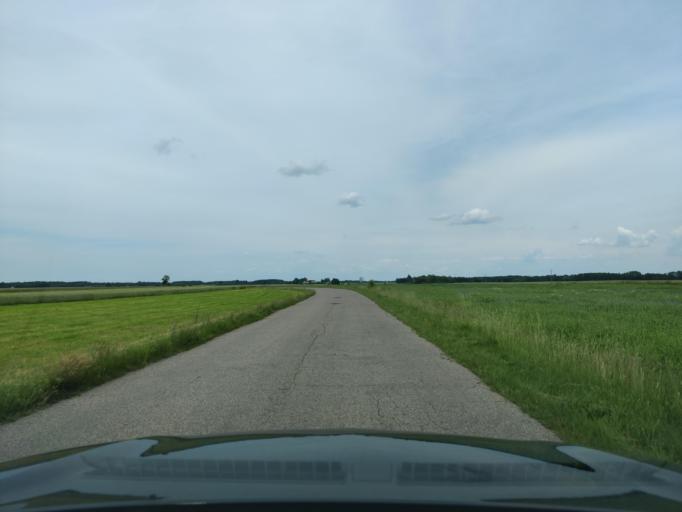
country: PL
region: Masovian Voivodeship
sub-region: Powiat pultuski
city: Obryte
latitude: 52.7208
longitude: 21.2390
